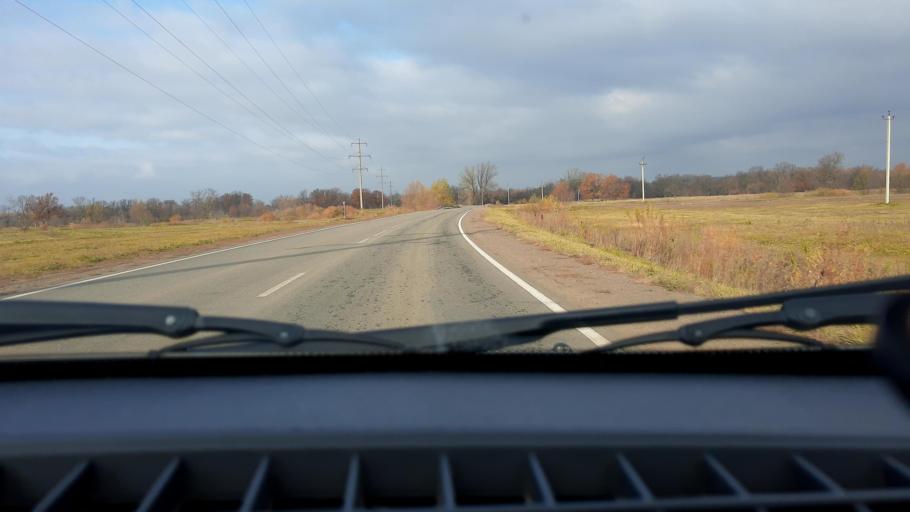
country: RU
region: Bashkortostan
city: Kabakovo
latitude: 54.5613
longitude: 55.9998
